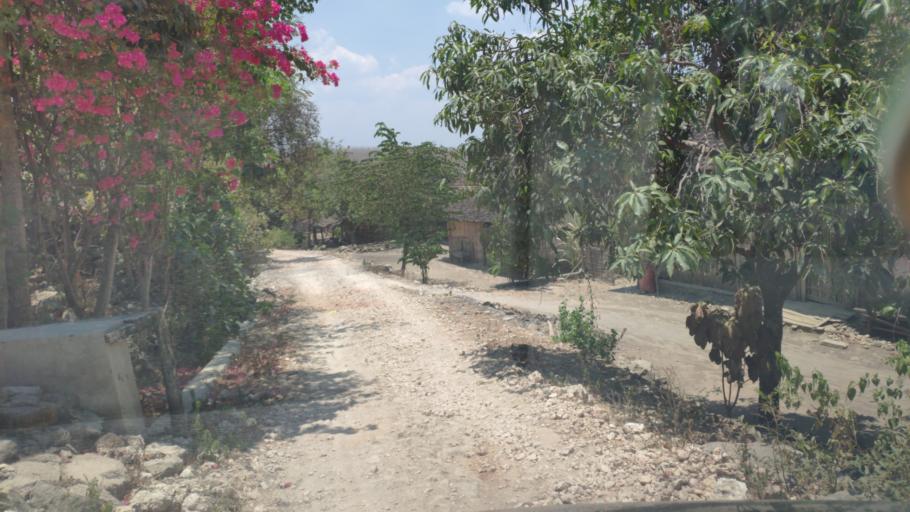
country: ID
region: West Java
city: Ngawi
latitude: -7.3266
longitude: 111.3494
